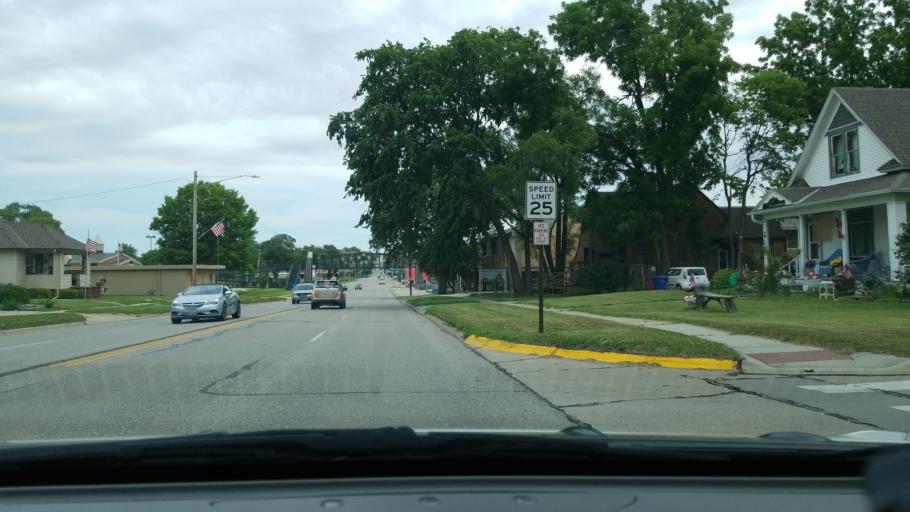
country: US
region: Nebraska
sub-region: Sarpy County
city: Papillion
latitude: 41.1516
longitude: -96.0429
